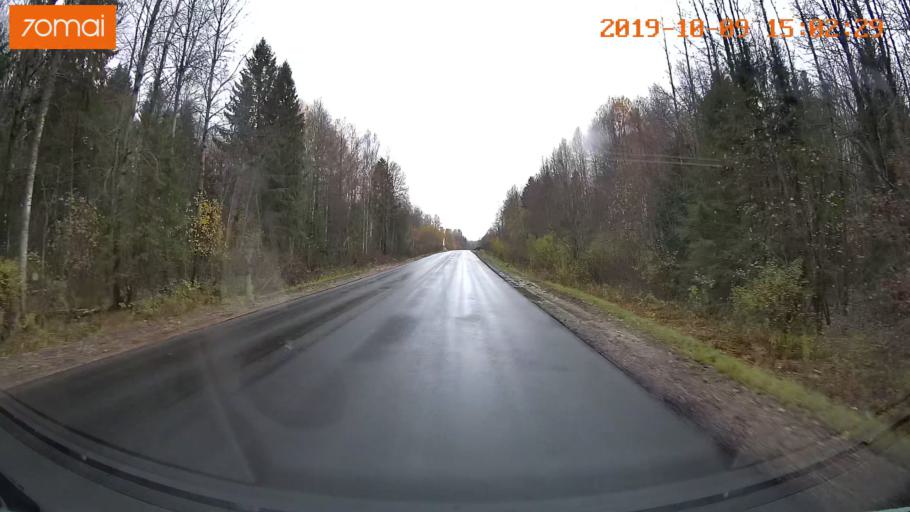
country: RU
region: Kostroma
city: Chistyye Bory
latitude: 58.2844
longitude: 41.6788
